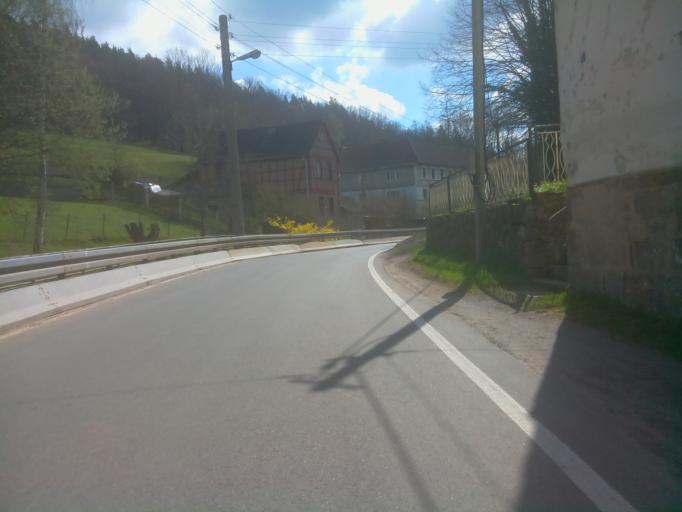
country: DE
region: Thuringia
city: Karlsdorf
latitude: 50.7969
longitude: 11.7984
